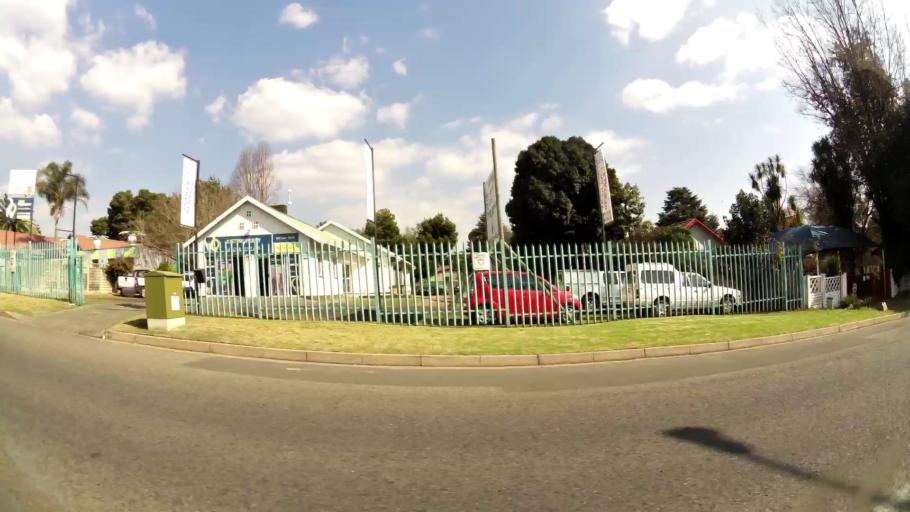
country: ZA
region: Gauteng
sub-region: City of Johannesburg Metropolitan Municipality
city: Modderfontein
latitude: -26.0901
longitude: 28.2500
